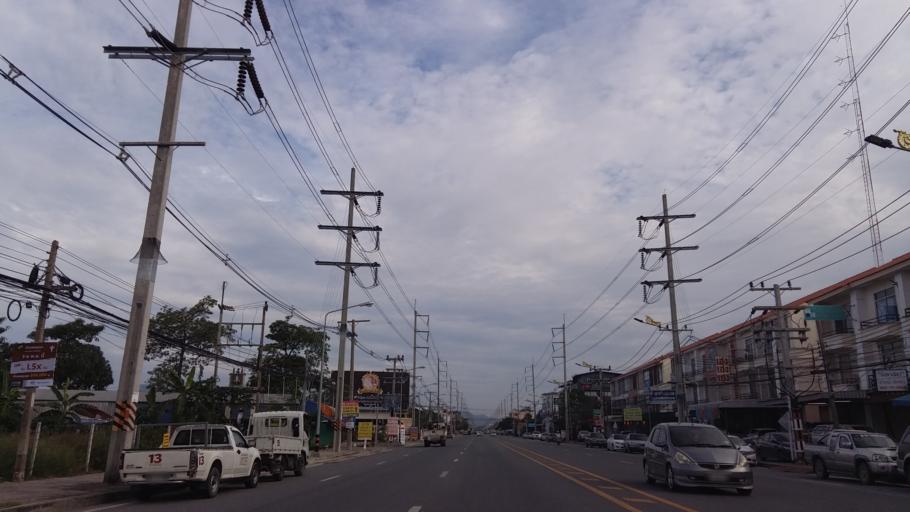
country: TH
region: Chon Buri
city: Chon Buri
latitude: 13.3318
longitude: 100.9356
